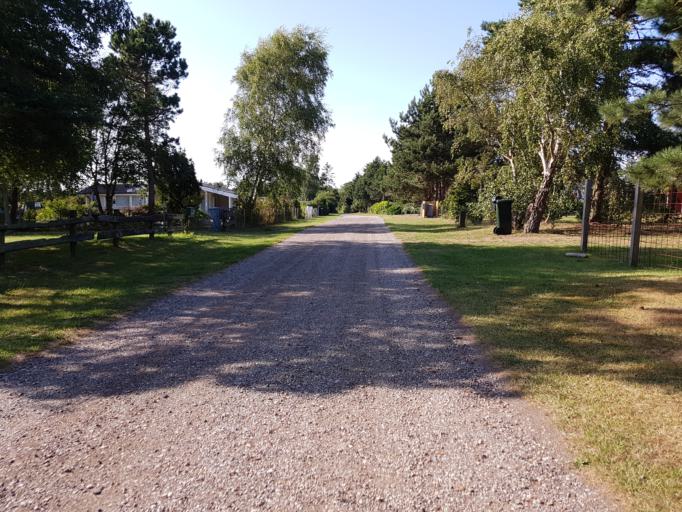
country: DK
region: Zealand
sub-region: Guldborgsund Kommune
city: Nykobing Falster
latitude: 54.5983
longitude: 11.9633
